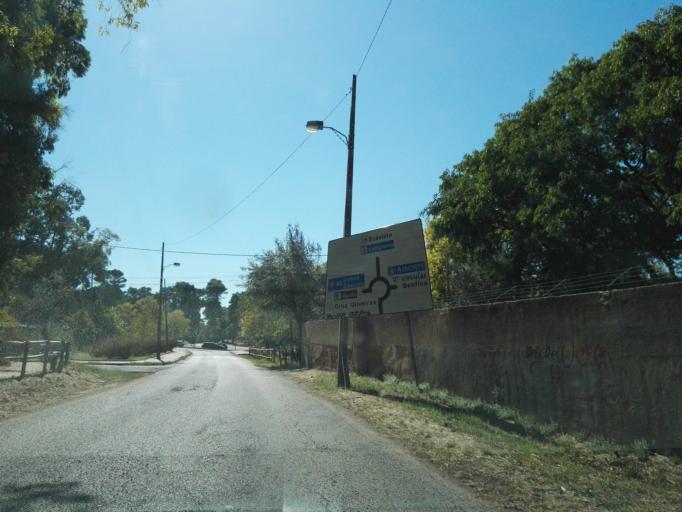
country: PT
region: Lisbon
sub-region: Odivelas
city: Pontinha
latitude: 38.7374
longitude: -9.2007
